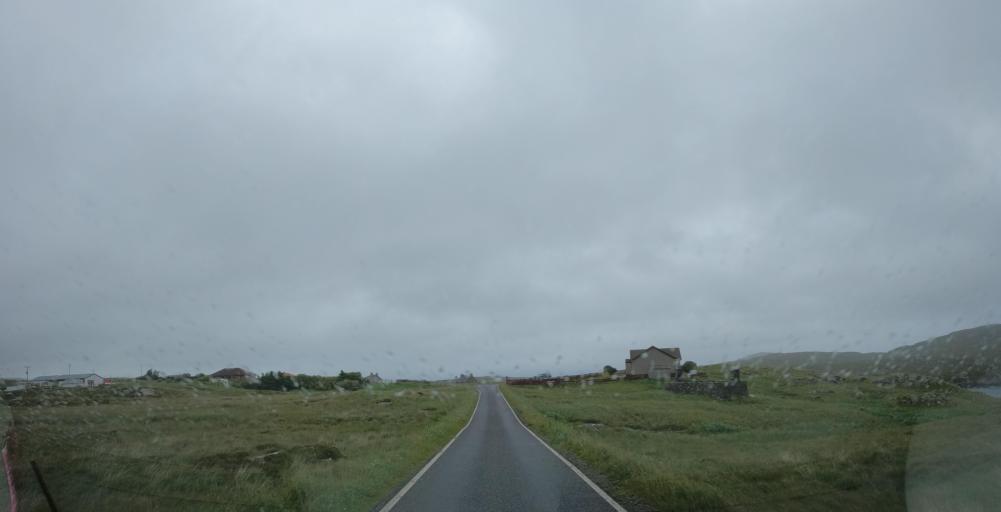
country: GB
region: Scotland
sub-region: Eilean Siar
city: Barra
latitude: 56.9842
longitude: -7.4111
